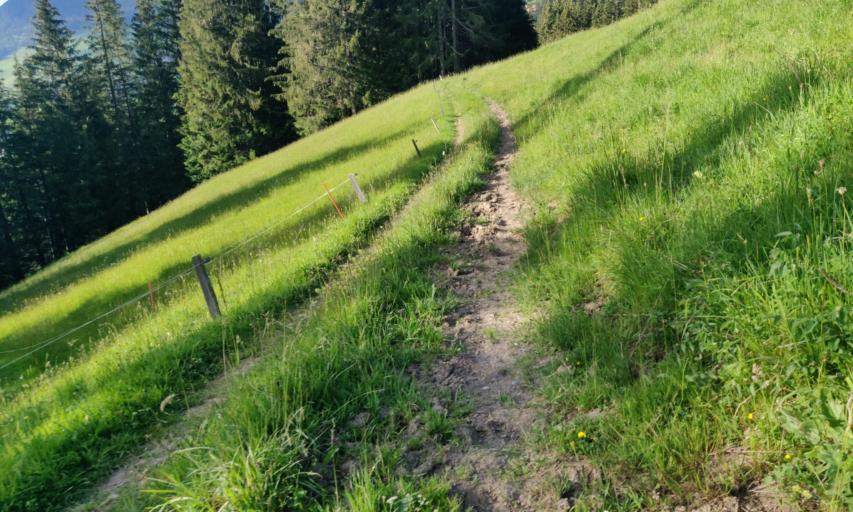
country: CH
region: Bern
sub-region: Obersimmental-Saanen District
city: Gstaad
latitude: 46.4053
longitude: 7.3379
